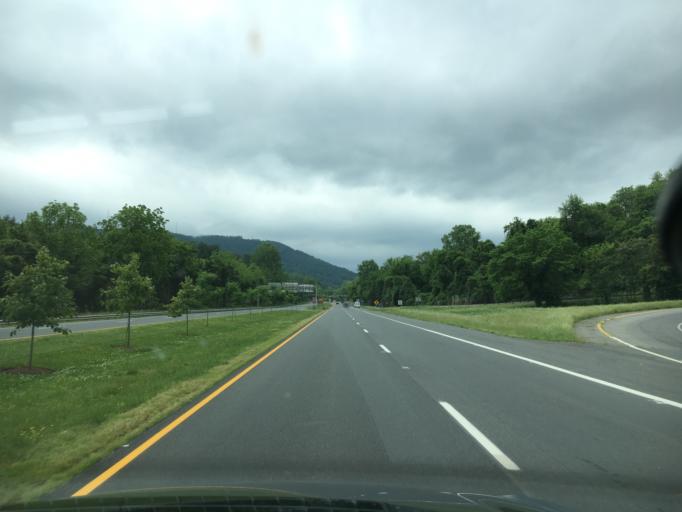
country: US
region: Virginia
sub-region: City of Charlottesville
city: Charlottesville
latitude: 38.0096
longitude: -78.4777
